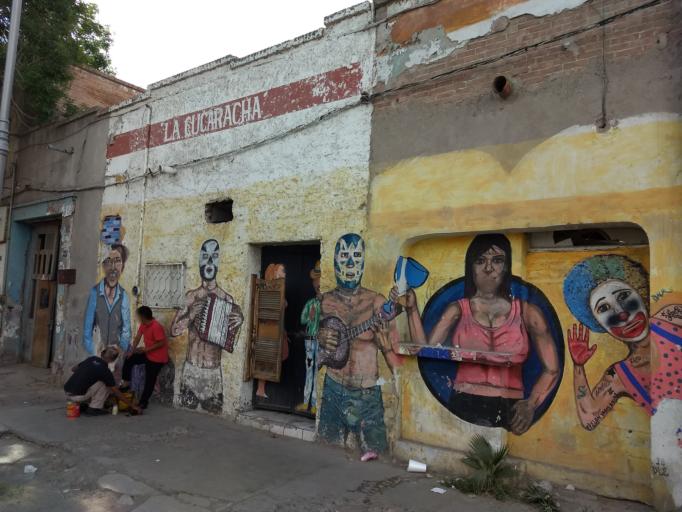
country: MX
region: Durango
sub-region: Lerdo
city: El Huarache (El Guarache)
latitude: 25.5381
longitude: -103.4667
